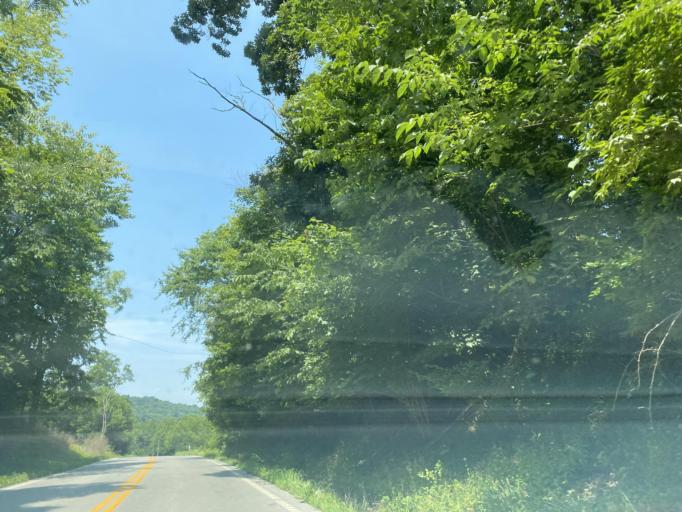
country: US
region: Kentucky
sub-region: Kenton County
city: Ryland Heights
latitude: 38.9064
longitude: -84.4475
